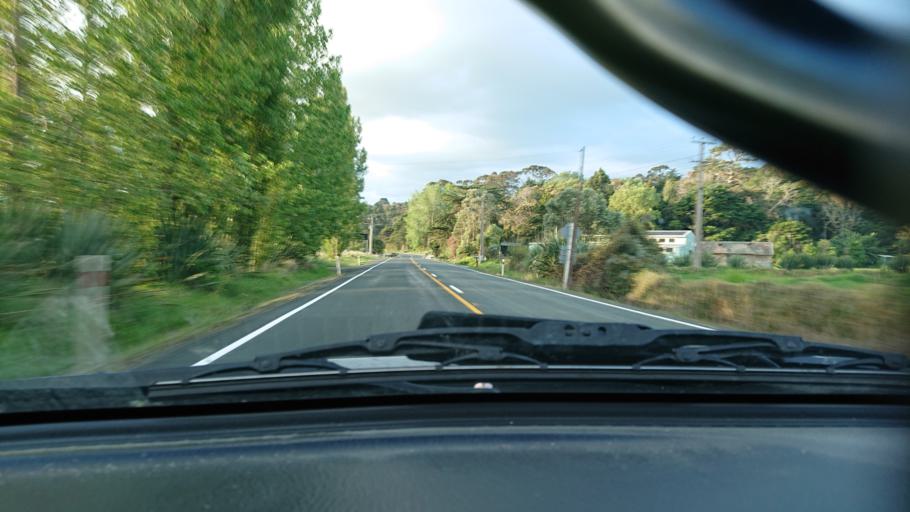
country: NZ
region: Auckland
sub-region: Auckland
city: Parakai
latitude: -36.5330
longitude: 174.4561
